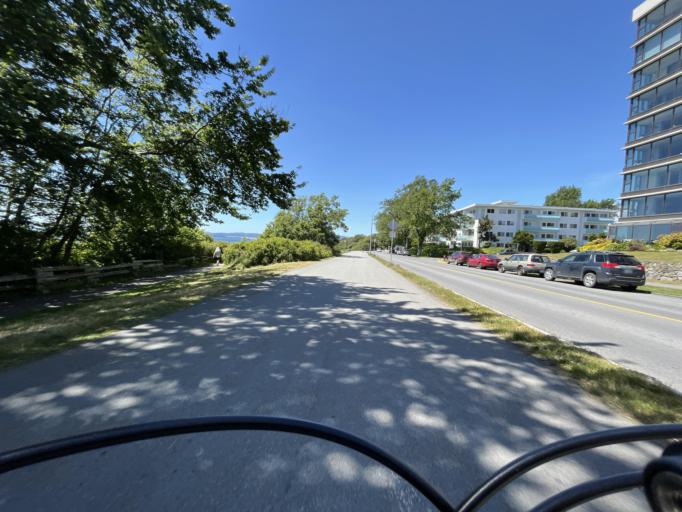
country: CA
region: British Columbia
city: Victoria
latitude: 48.4088
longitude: -123.3702
